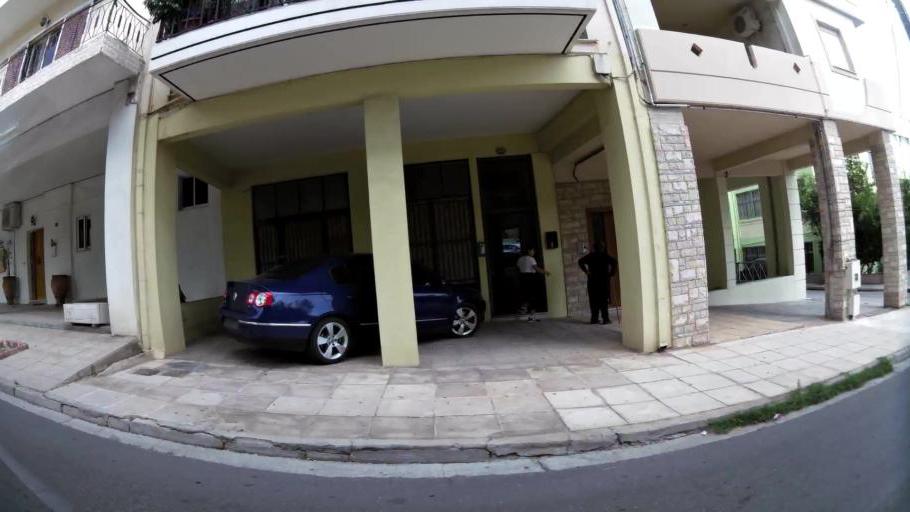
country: GR
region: Attica
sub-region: Nomarchia Athinas
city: Petroupolis
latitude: 38.0447
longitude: 23.6960
